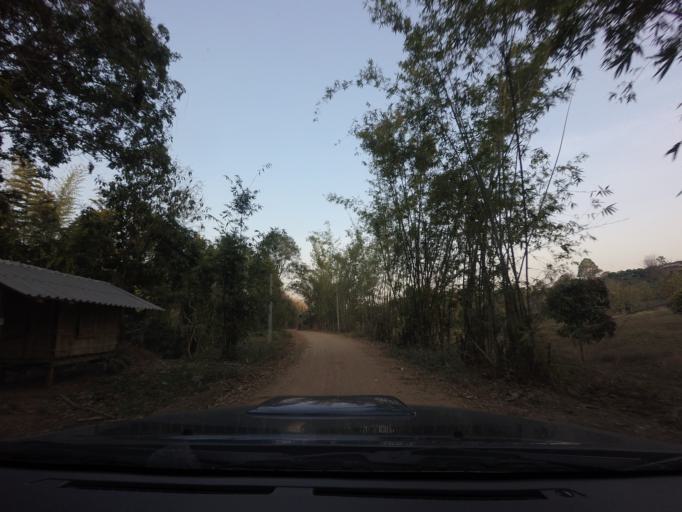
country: TH
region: Chiang Mai
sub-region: Amphoe Chiang Dao
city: Chiang Dao
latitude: 19.3630
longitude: 98.9310
